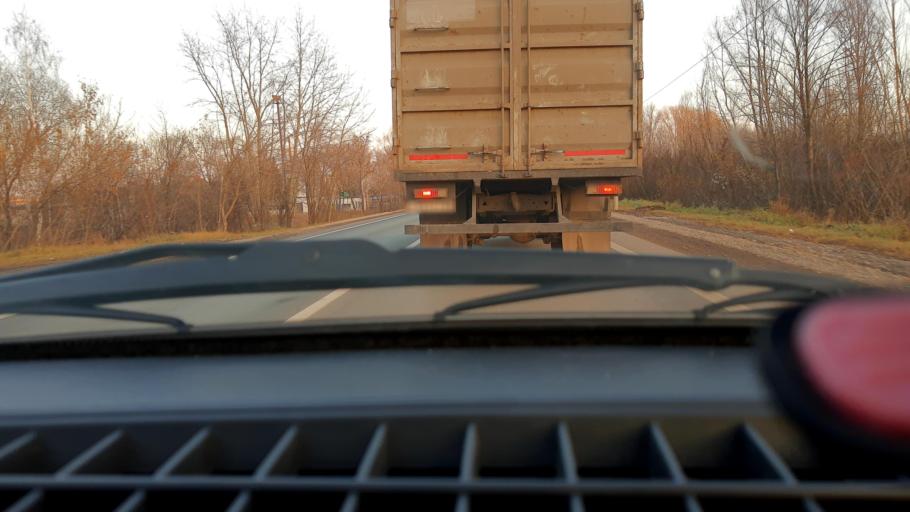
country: RU
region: Bashkortostan
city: Ufa
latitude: 54.8393
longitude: 56.1265
